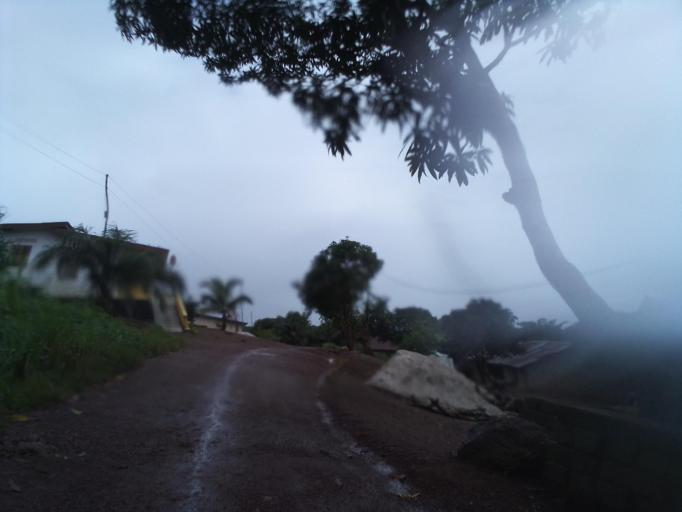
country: SL
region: Eastern Province
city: Kenema
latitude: 7.8538
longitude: -11.1956
